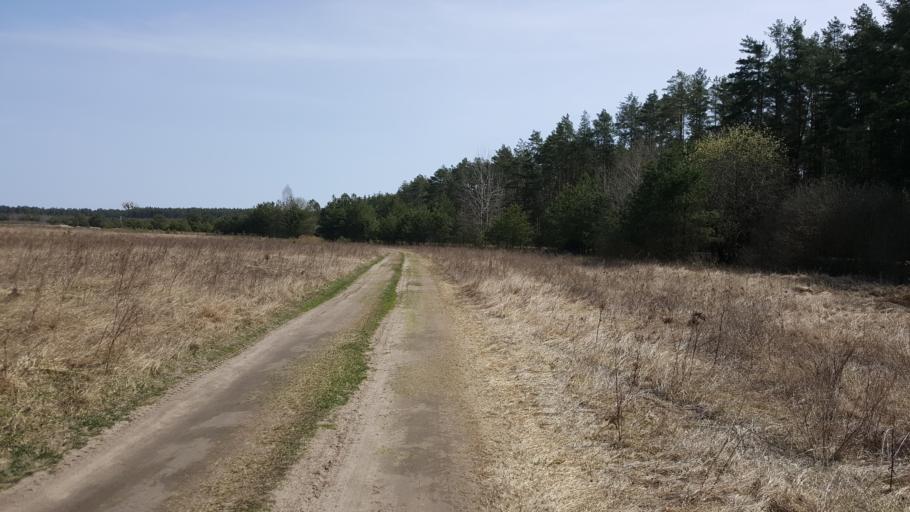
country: BY
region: Brest
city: Kamyanyuki
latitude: 52.5632
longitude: 23.7612
